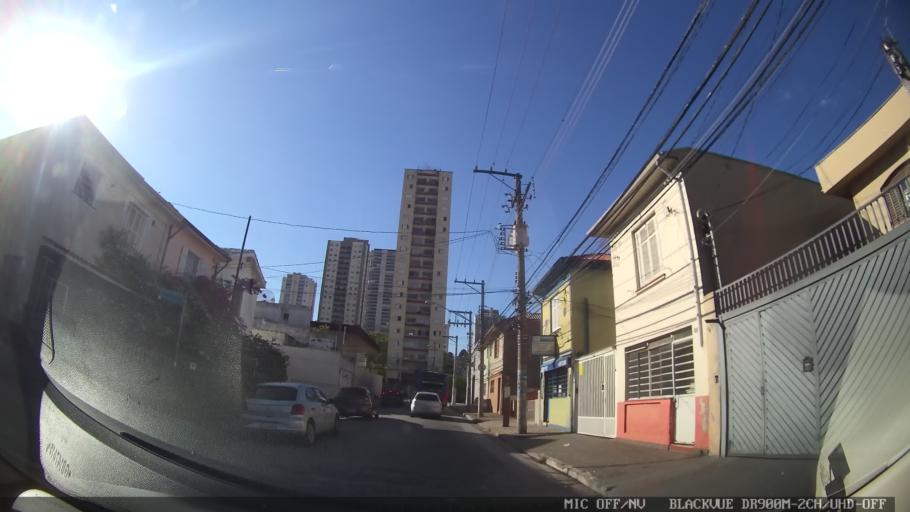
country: BR
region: Sao Paulo
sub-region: Sao Paulo
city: Sao Paulo
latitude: -23.5009
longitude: -46.6350
